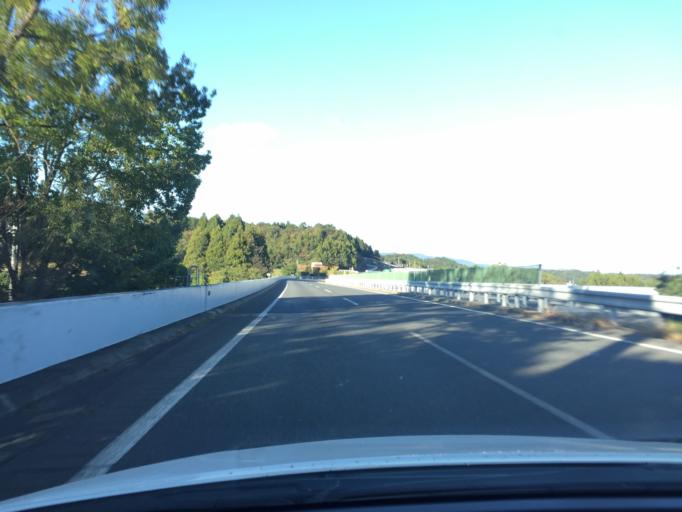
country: JP
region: Fukushima
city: Iwaki
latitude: 37.0602
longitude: 140.8317
